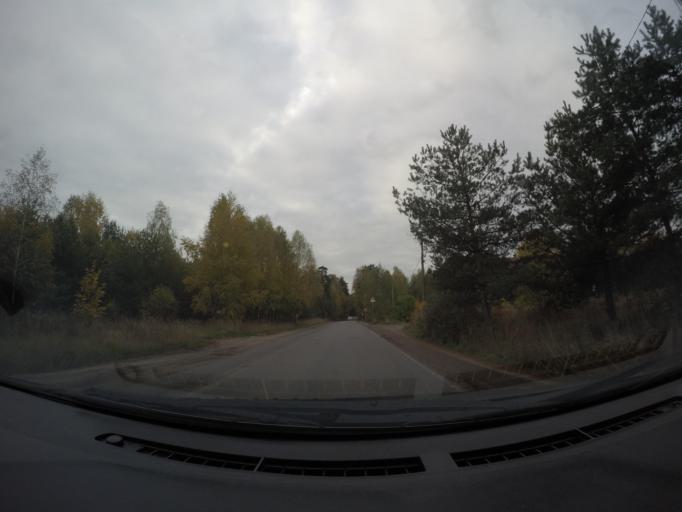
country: RU
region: Moskovskaya
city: Vishnyakovskiye Dachi
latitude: 55.8120
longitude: 38.1094
